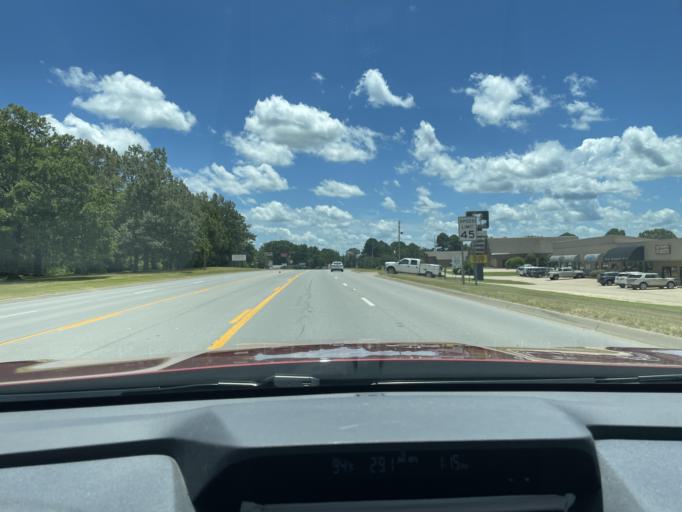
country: US
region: Arkansas
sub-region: Drew County
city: Monticello
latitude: 33.6477
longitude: -91.8014
